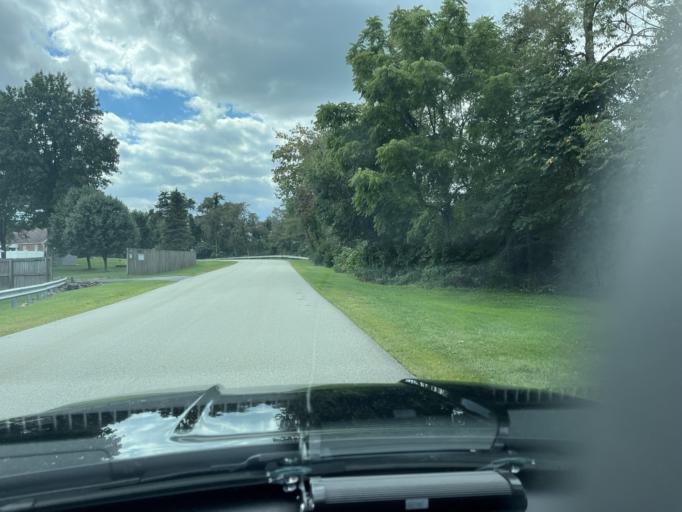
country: US
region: Pennsylvania
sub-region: Fayette County
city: South Uniontown
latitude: 39.8955
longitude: -79.7524
